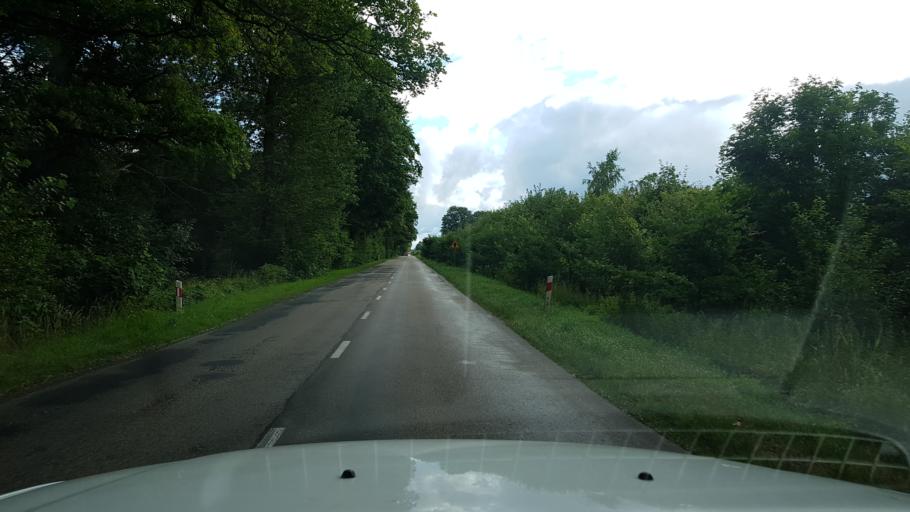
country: PL
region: West Pomeranian Voivodeship
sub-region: Powiat swidwinski
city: Rabino
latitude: 53.7778
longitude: 15.9827
